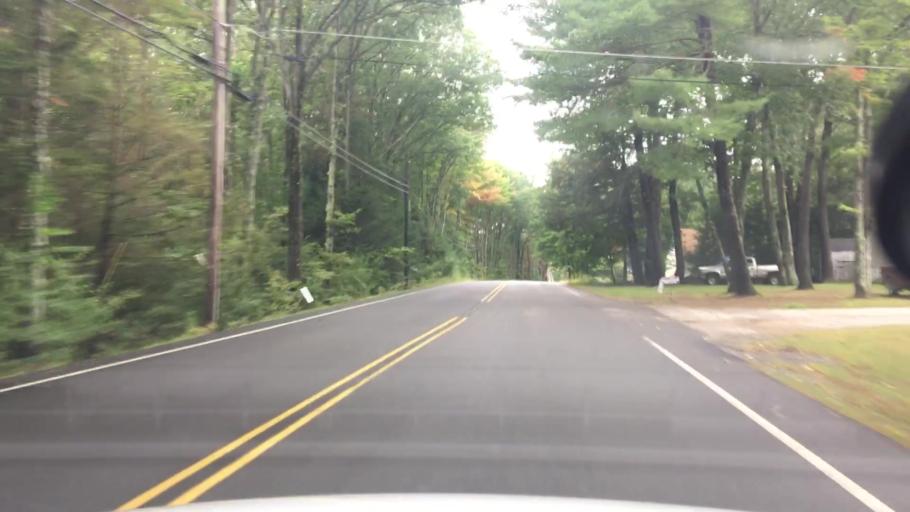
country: US
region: New Hampshire
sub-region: Strafford County
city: Rochester
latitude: 43.2848
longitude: -70.9584
